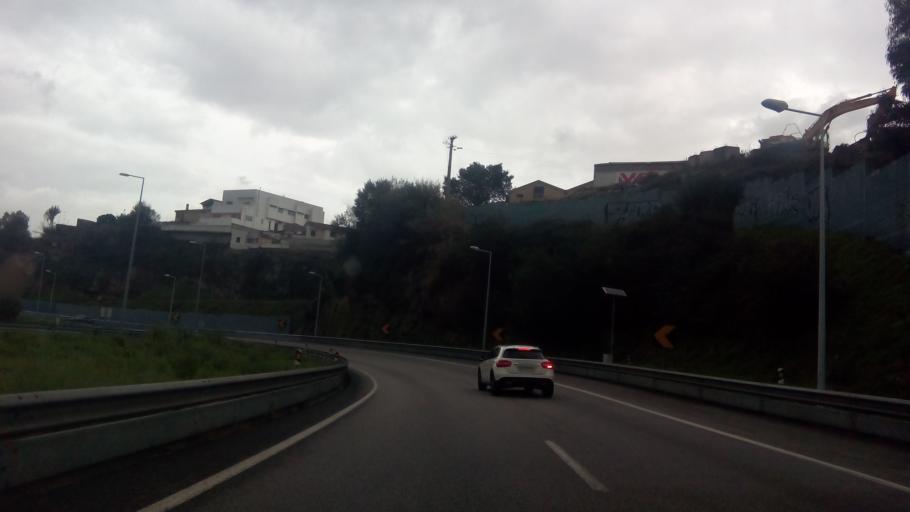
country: PT
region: Porto
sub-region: Maia
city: Pedroucos
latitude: 41.1950
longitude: -8.5893
